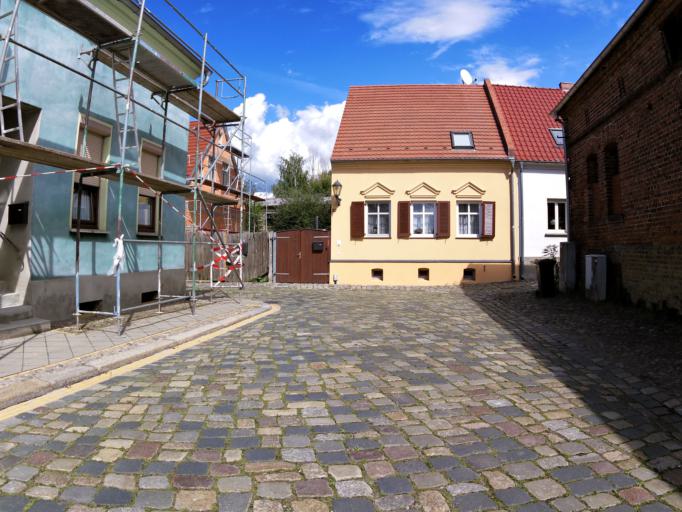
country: DE
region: Brandenburg
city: Storkow
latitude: 52.2562
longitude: 13.9313
